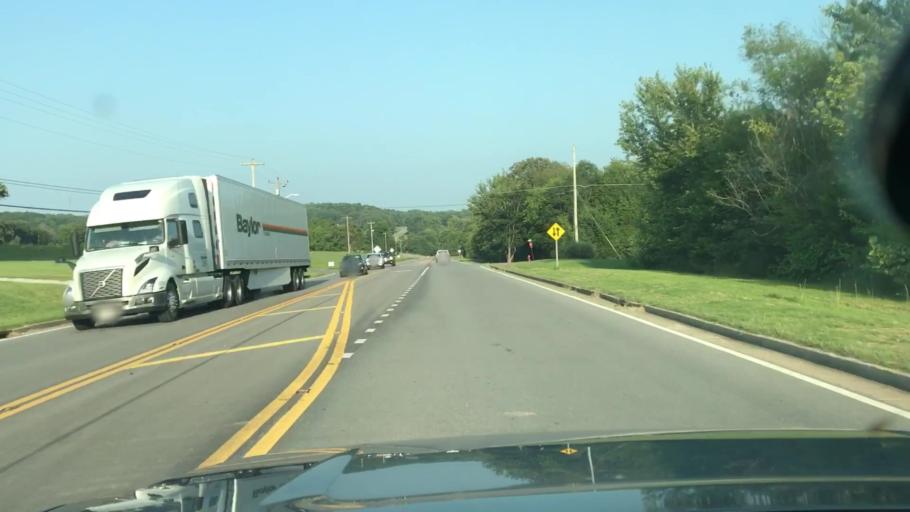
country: US
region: Tennessee
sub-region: Sumner County
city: Portland
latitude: 36.5789
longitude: -86.4659
